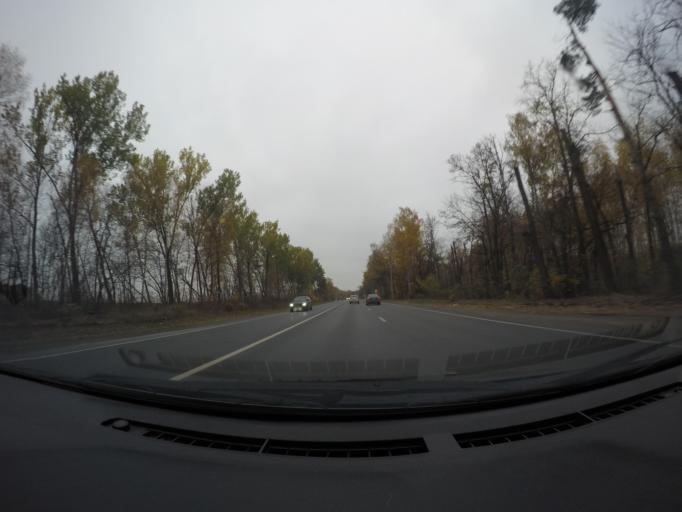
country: RU
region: Moskovskaya
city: Malyshevo
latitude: 55.4499
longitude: 38.3239
